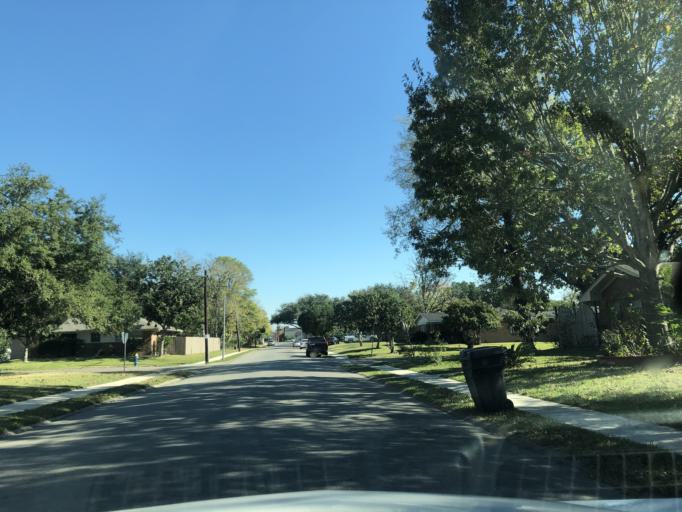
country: US
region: Texas
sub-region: Harris County
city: Bellaire
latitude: 29.6973
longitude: -95.4955
